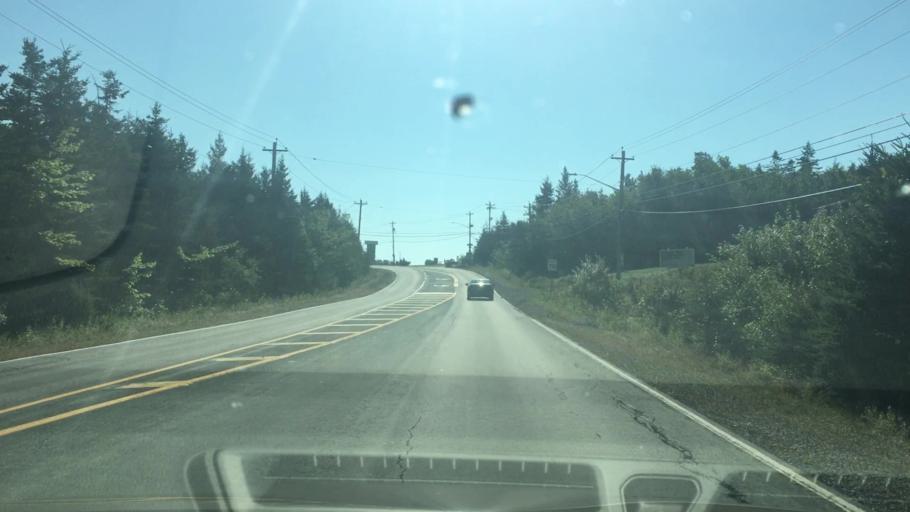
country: CA
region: Nova Scotia
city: Cole Harbour
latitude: 44.7793
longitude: -63.0938
